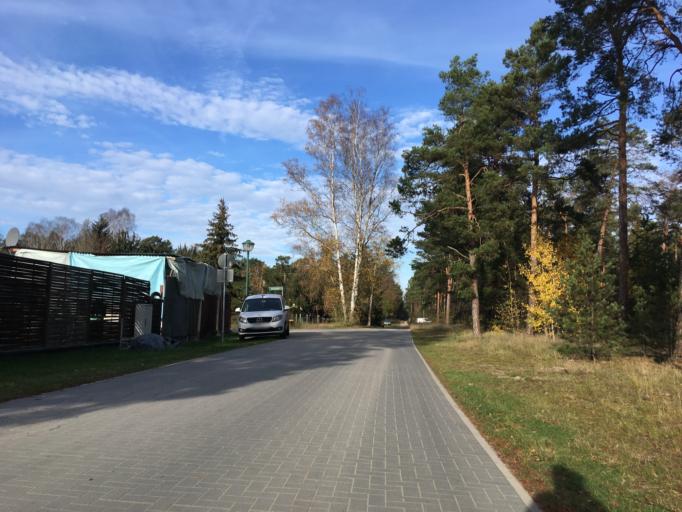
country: DE
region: Brandenburg
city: Halbe
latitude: 52.1155
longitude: 13.7010
